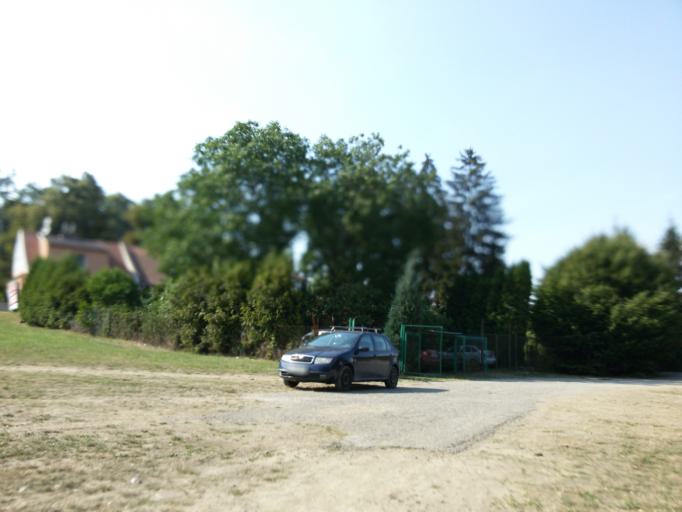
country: CZ
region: South Moravian
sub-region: Mesto Brno
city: Mokra Hora
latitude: 49.2516
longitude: 16.5902
